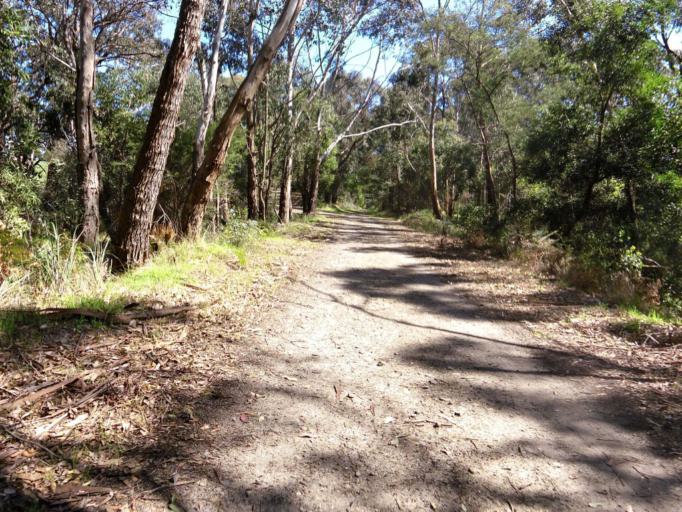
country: AU
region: Victoria
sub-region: Latrobe
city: Moe
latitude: -38.1690
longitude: 146.3192
